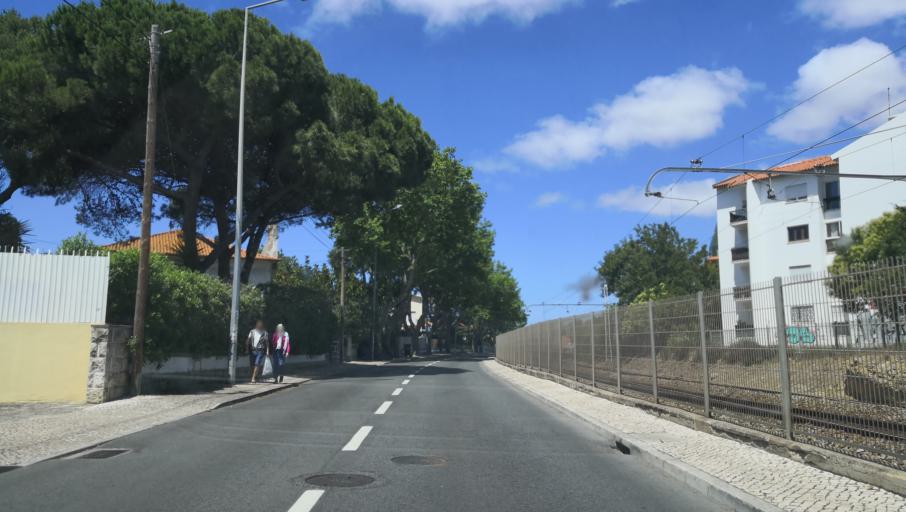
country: PT
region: Lisbon
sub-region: Cascais
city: Parede
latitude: 38.6874
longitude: -9.3493
